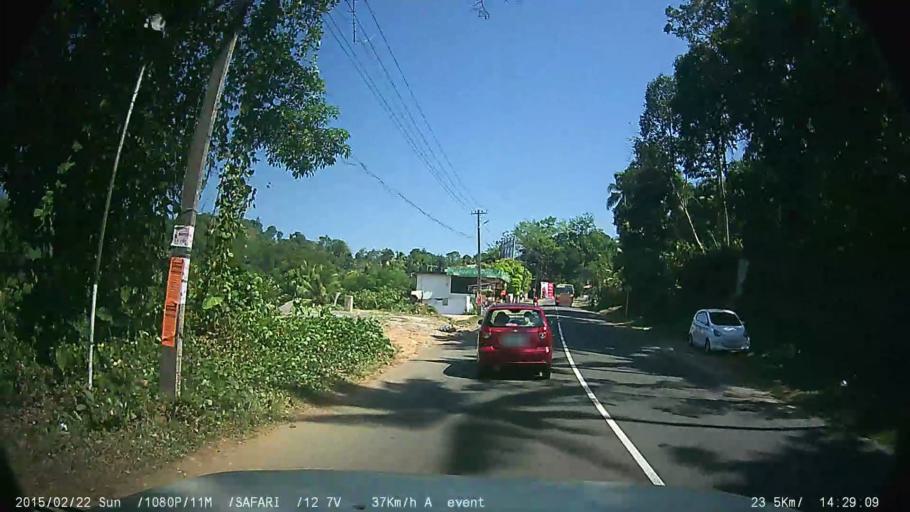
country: IN
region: Kerala
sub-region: Kottayam
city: Erattupetta
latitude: 9.5670
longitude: 76.7418
